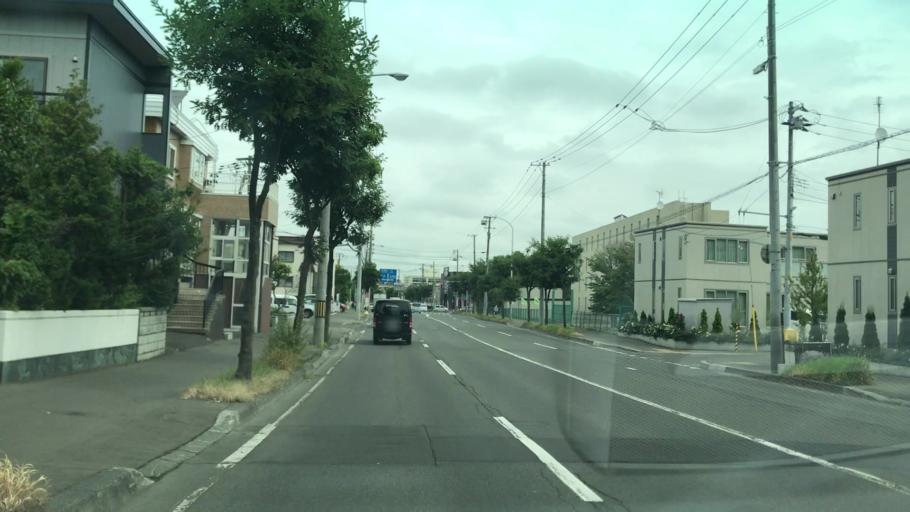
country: JP
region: Hokkaido
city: Sapporo
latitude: 43.0927
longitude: 141.3016
